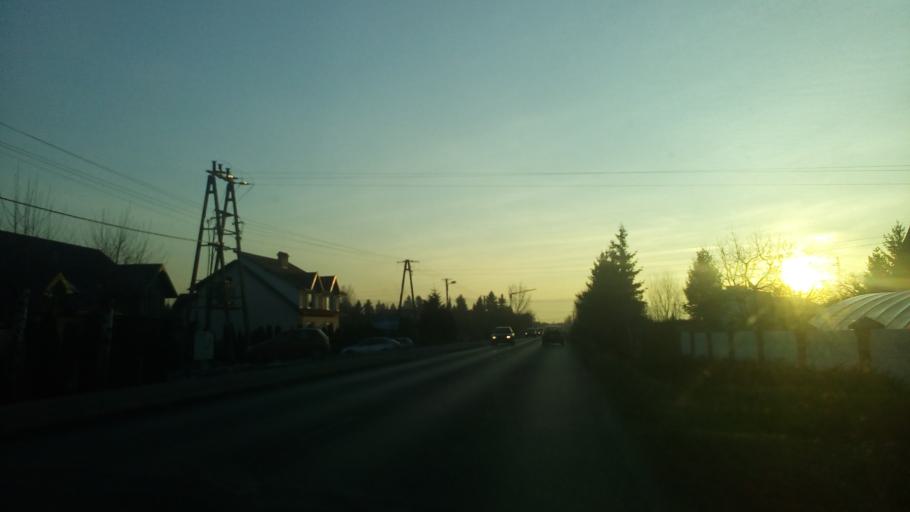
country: PL
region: Lesser Poland Voivodeship
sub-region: Powiat nowosadecki
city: Chelmiec
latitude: 49.6163
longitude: 20.6647
